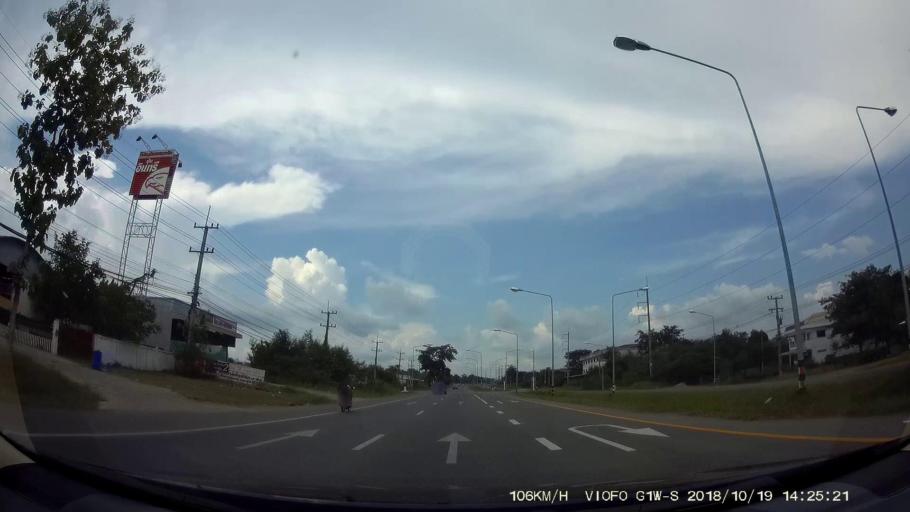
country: TH
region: Chaiyaphum
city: Kaeng Khro
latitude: 16.0925
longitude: 102.2658
